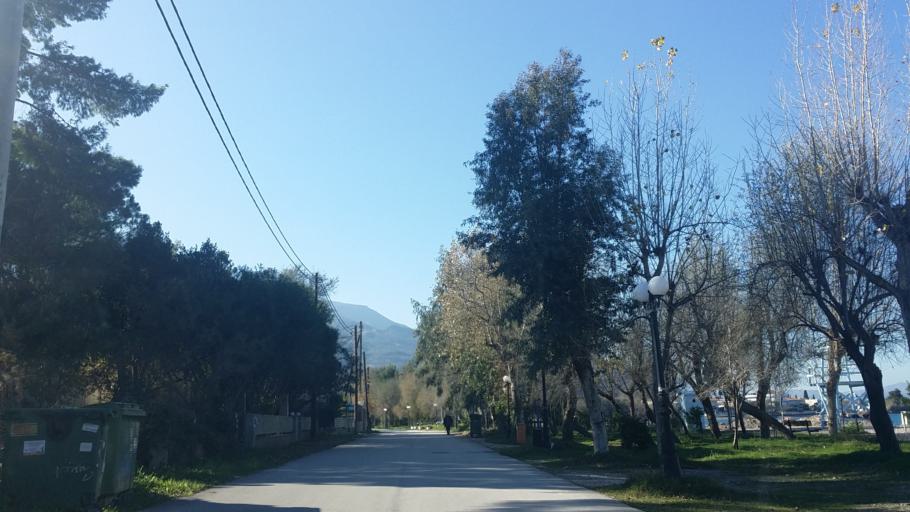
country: GR
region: West Greece
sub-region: Nomos Achaias
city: Temeni
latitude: 38.2003
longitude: 22.1793
